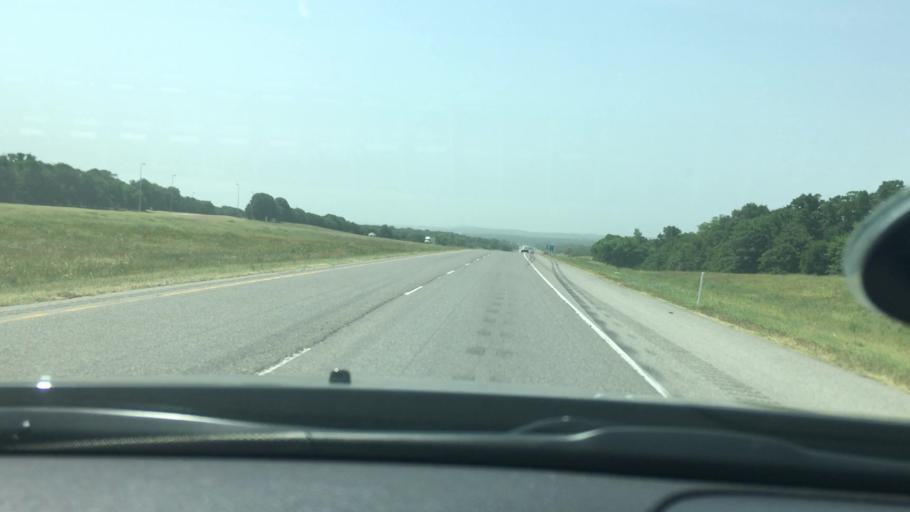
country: US
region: Oklahoma
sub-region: Murray County
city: Davis
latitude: 34.5548
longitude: -97.1922
